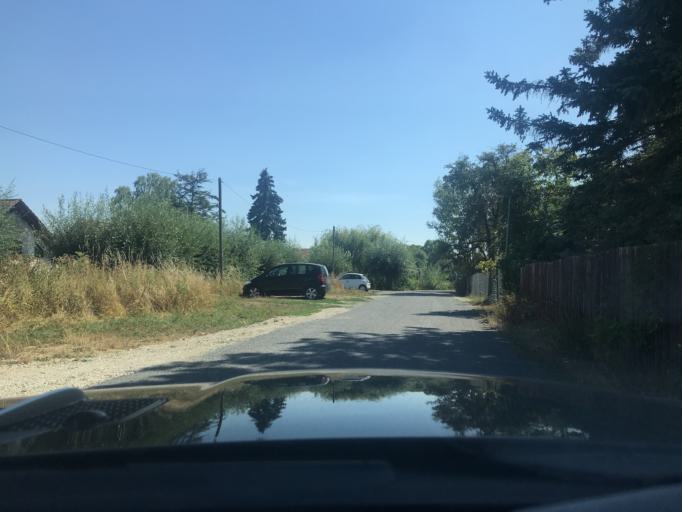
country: DE
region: Thuringia
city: Muehlhausen
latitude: 51.2170
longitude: 10.4404
